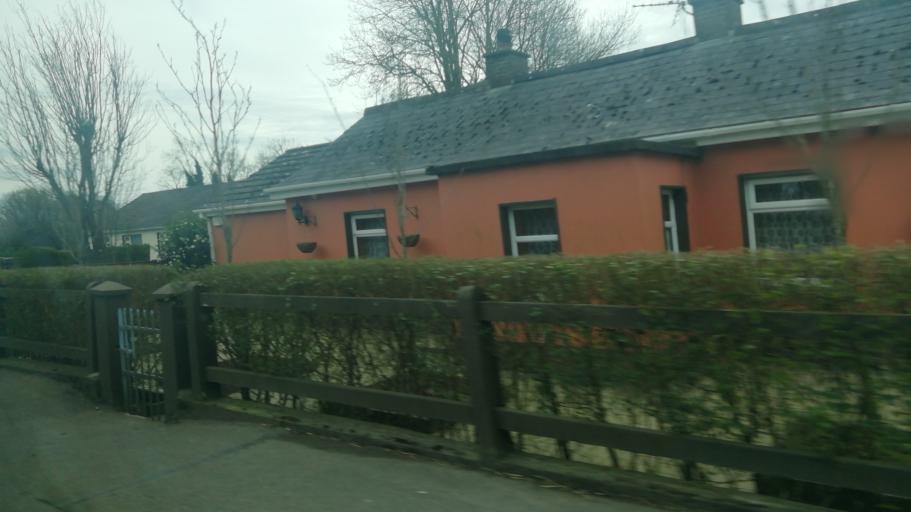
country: IE
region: Leinster
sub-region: Kildare
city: Derrinturn
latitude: 53.3439
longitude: -6.9475
